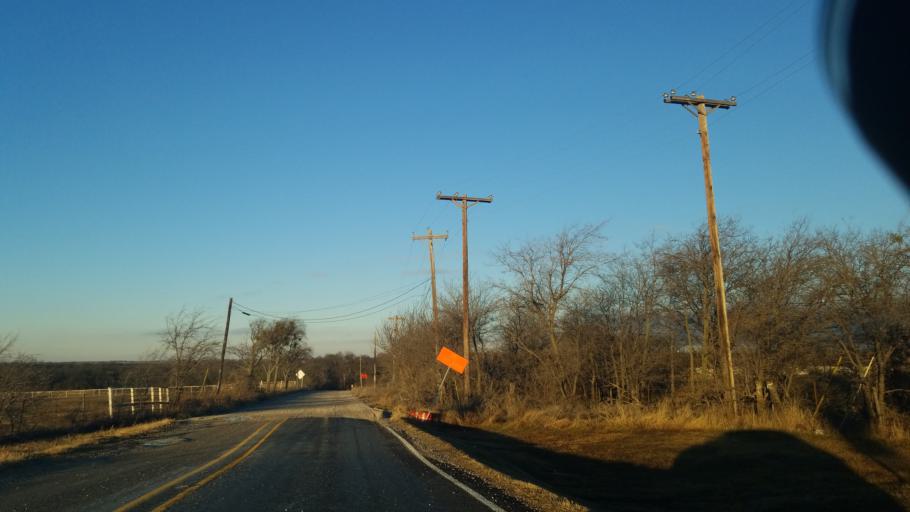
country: US
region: Texas
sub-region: Denton County
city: Justin
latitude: 33.0647
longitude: -97.2452
